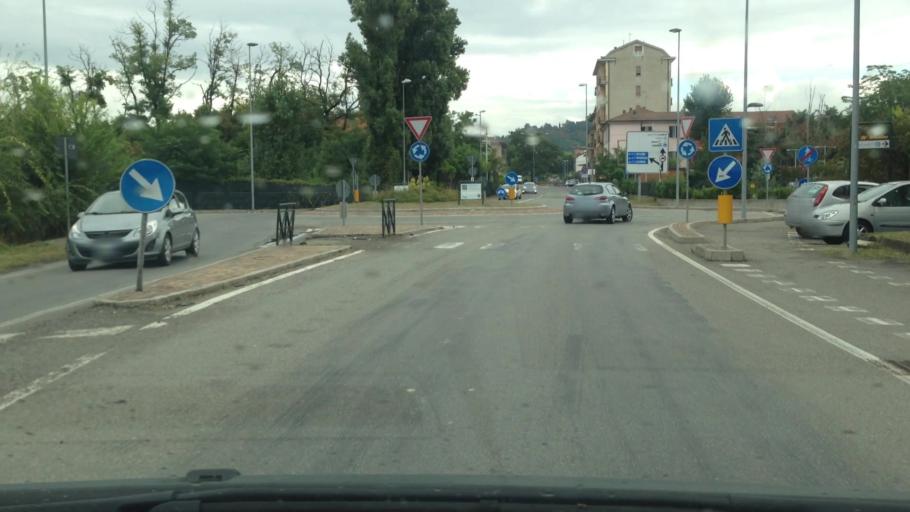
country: IT
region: Piedmont
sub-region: Provincia di Alessandria
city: Tortona
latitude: 44.8948
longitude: 8.8505
